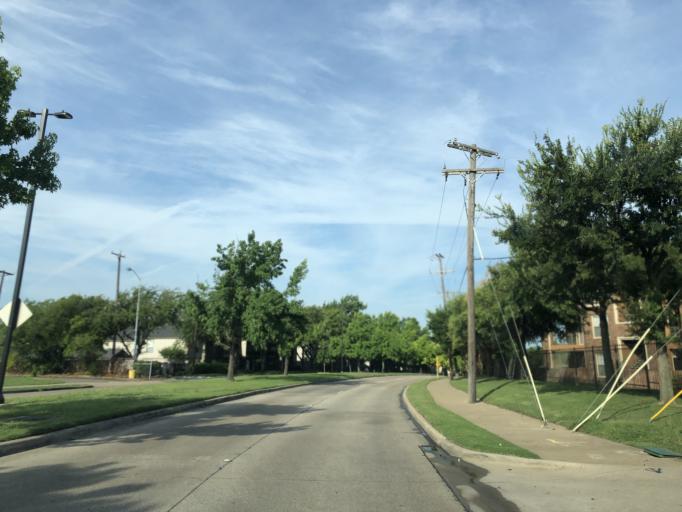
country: US
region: Texas
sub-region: Dallas County
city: Sunnyvale
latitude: 32.8454
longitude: -96.5974
